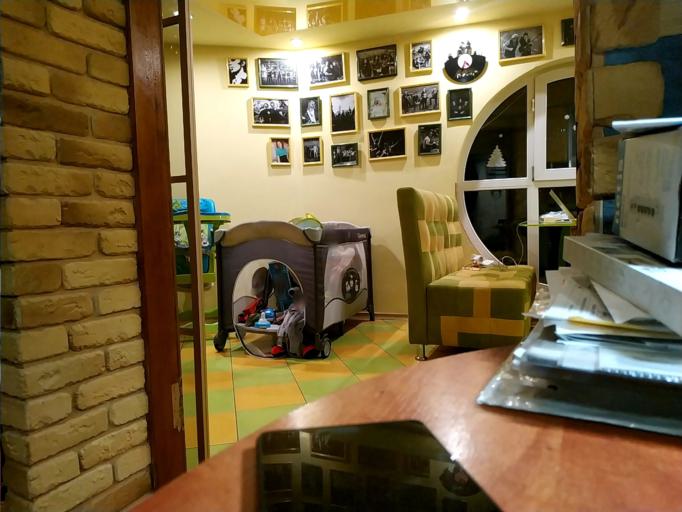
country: RU
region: Orjol
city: Naryshkino
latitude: 53.0161
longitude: 35.6912
